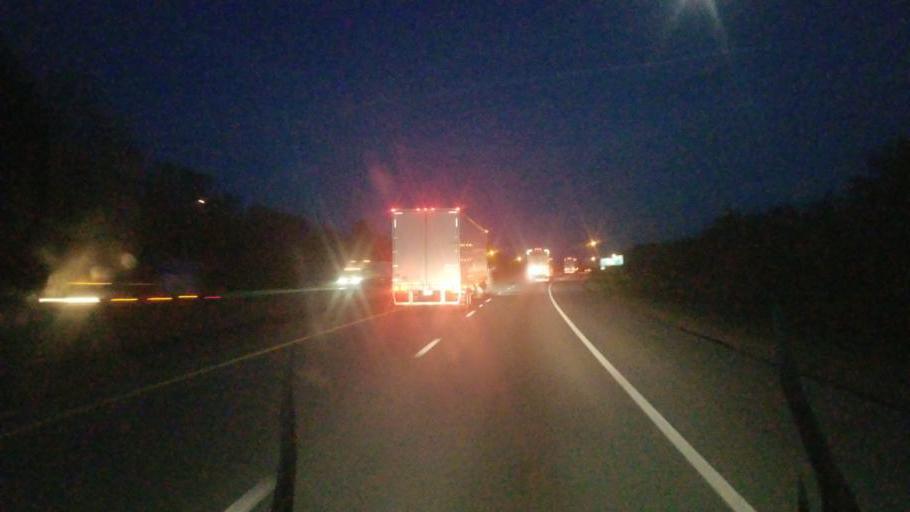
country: US
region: Ohio
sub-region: Belmont County
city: Barnesville
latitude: 40.0570
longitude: -81.2373
